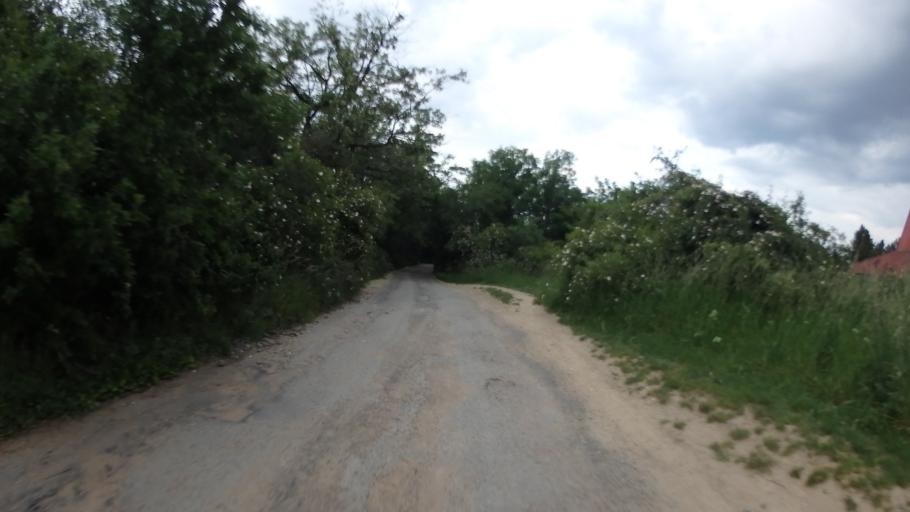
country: CZ
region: South Moravian
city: Ostopovice
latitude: 49.1371
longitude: 16.5470
